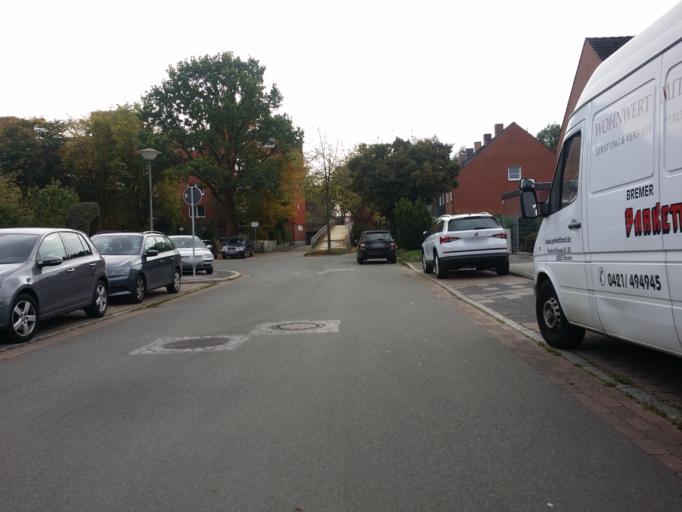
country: DE
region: Bremen
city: Bremen
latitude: 53.0310
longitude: 8.8221
